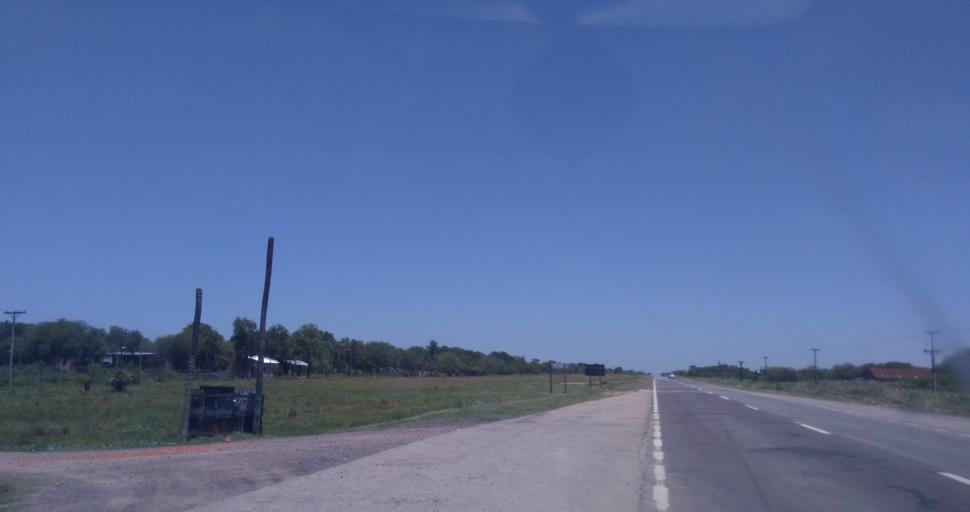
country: AR
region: Chaco
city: Fontana
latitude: -27.4741
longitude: -59.0548
